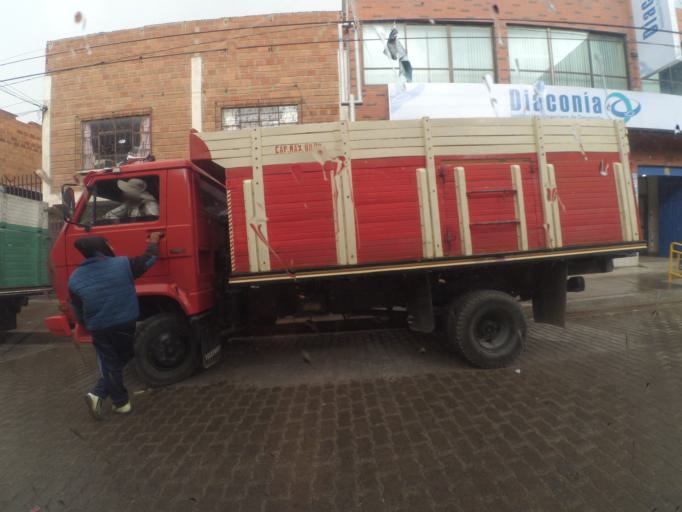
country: BO
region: La Paz
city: La Paz
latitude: -16.5106
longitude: -68.1635
